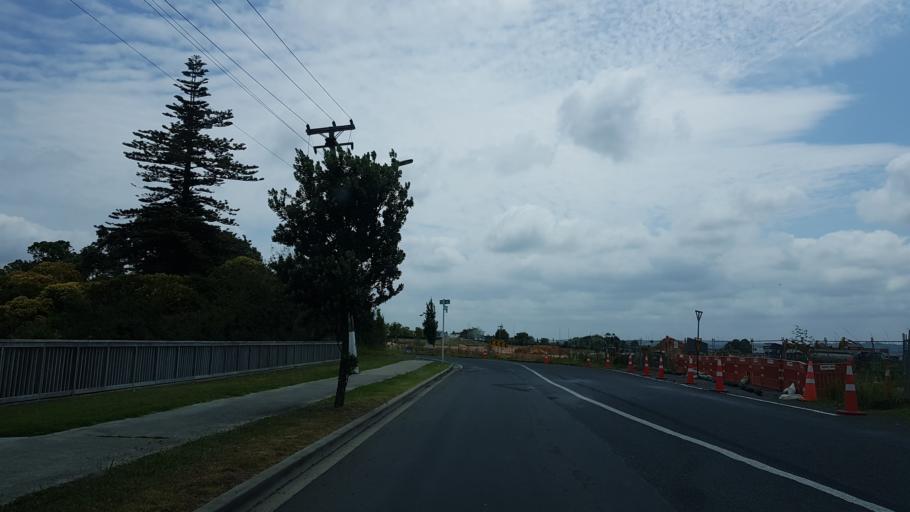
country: NZ
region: Auckland
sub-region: Auckland
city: Rosebank
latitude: -36.7994
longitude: 174.6537
